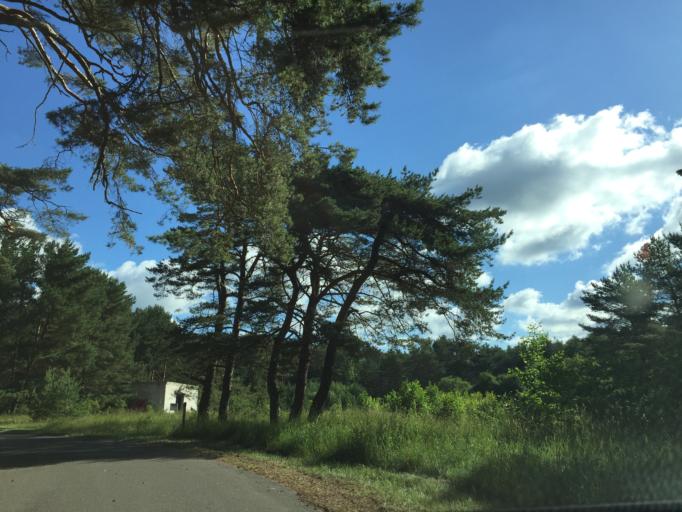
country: LV
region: Ventspils
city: Ventspils
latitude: 57.4444
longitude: 21.6056
